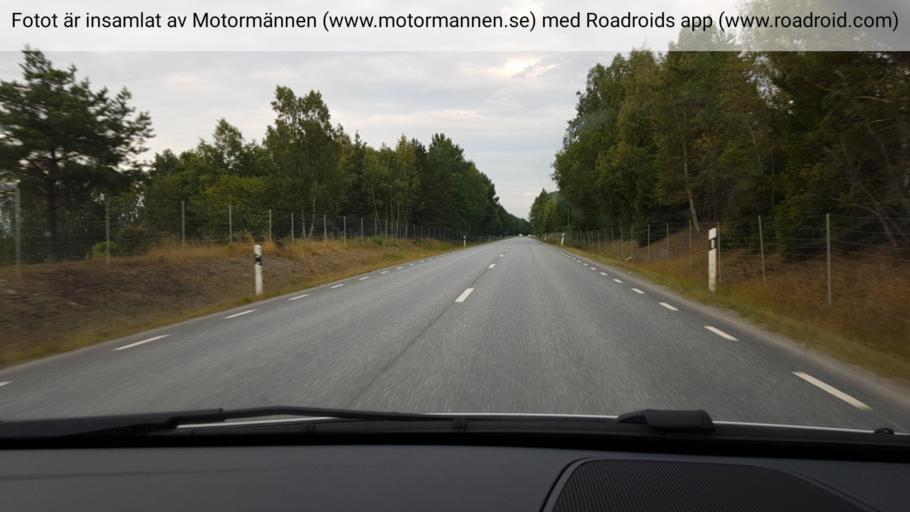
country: SE
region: Stockholm
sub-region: Upplands-Bro Kommun
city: Bro
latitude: 59.5899
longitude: 17.6218
